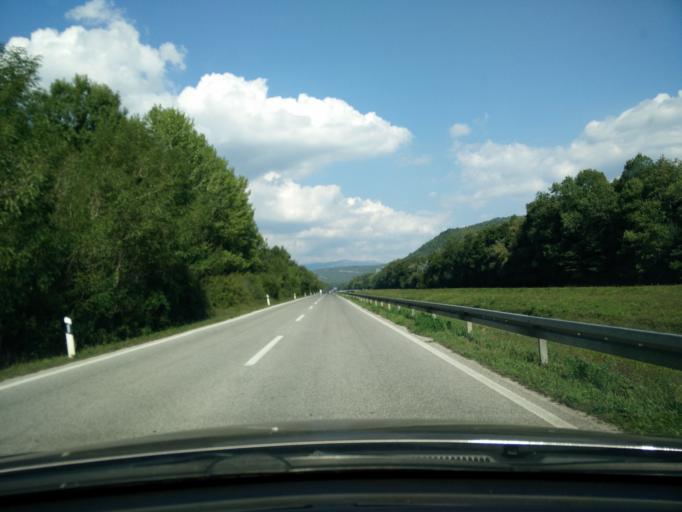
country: HR
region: Istarska
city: Karojba
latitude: 45.3530
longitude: 13.8510
